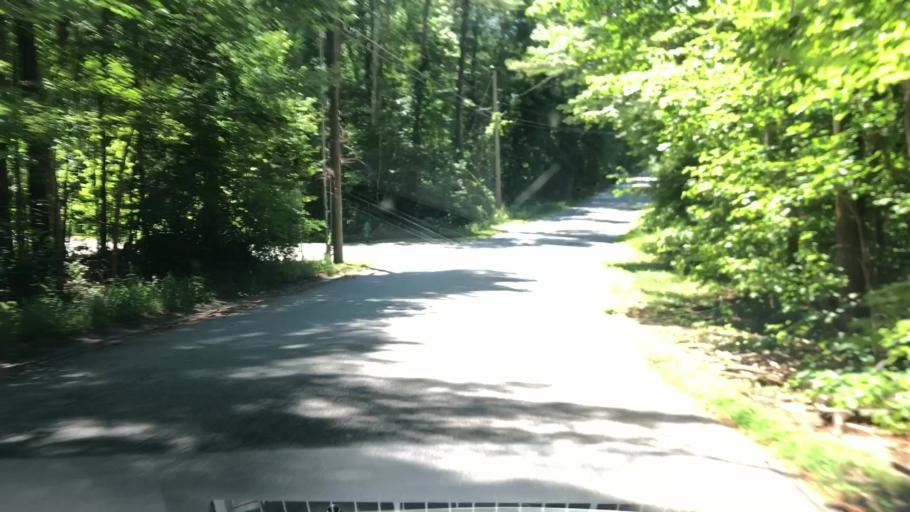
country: US
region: New Hampshire
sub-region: Hillsborough County
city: Milford
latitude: 42.8329
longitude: -71.5860
